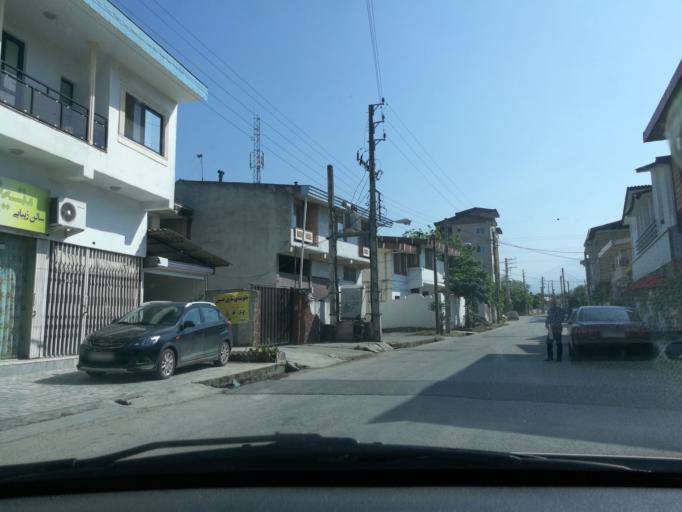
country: IR
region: Mazandaran
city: Chalus
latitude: 36.6634
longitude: 51.4310
